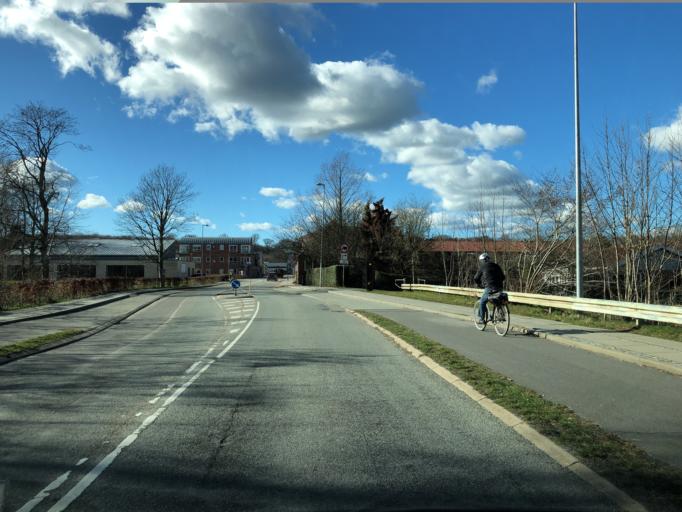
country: DK
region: Central Jutland
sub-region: Favrskov Kommune
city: Hinnerup
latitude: 56.2628
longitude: 10.0653
